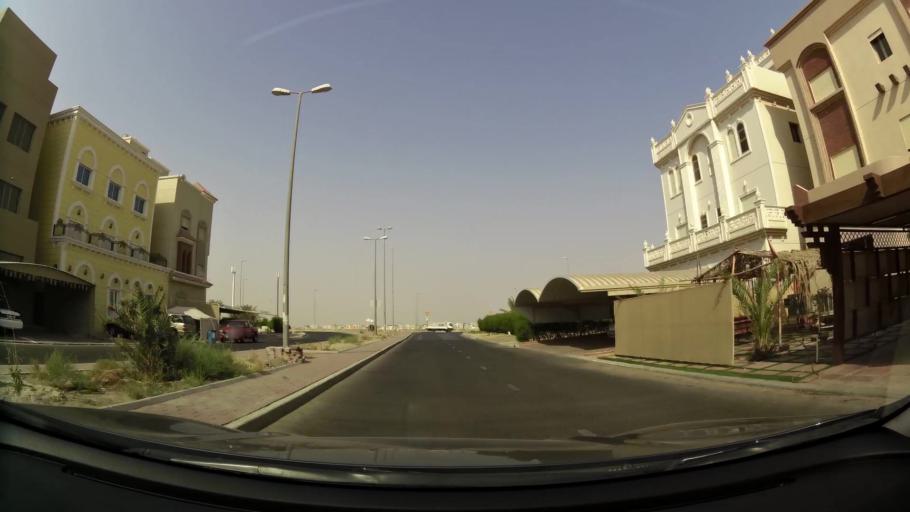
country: KW
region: Muhafazat al Jahra'
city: Al Jahra'
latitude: 29.3373
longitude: 47.7614
